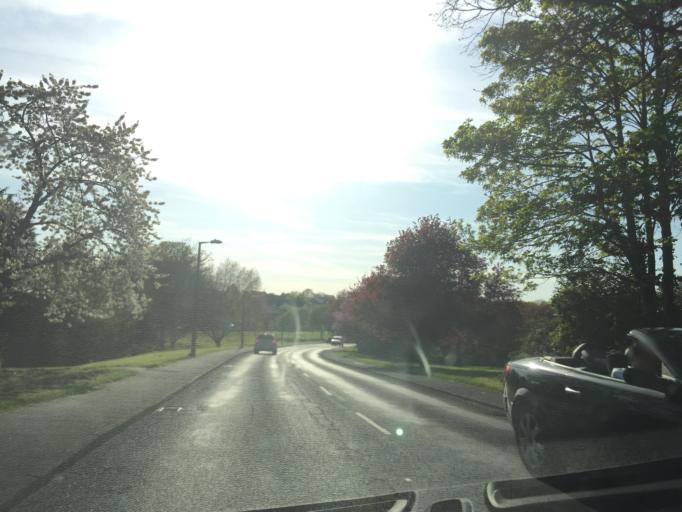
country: GB
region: England
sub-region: Essex
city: Harlow
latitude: 51.7461
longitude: 0.0894
